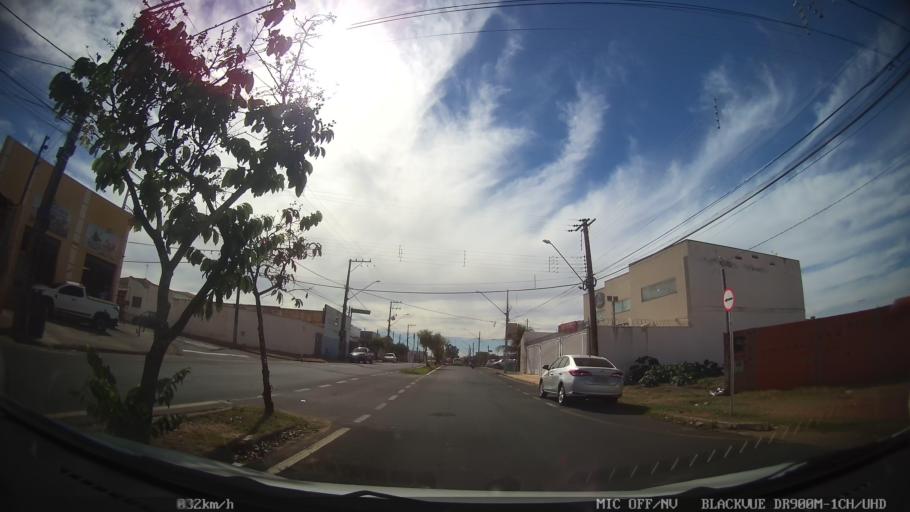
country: BR
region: Sao Paulo
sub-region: Catanduva
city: Catanduva
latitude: -21.1227
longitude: -48.9455
